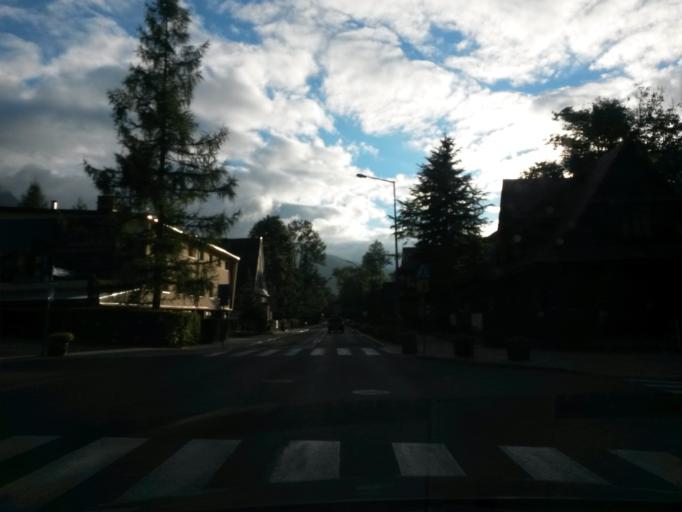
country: PL
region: Lesser Poland Voivodeship
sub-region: Powiat tatrzanski
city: Zakopane
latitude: 49.2902
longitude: 19.9590
